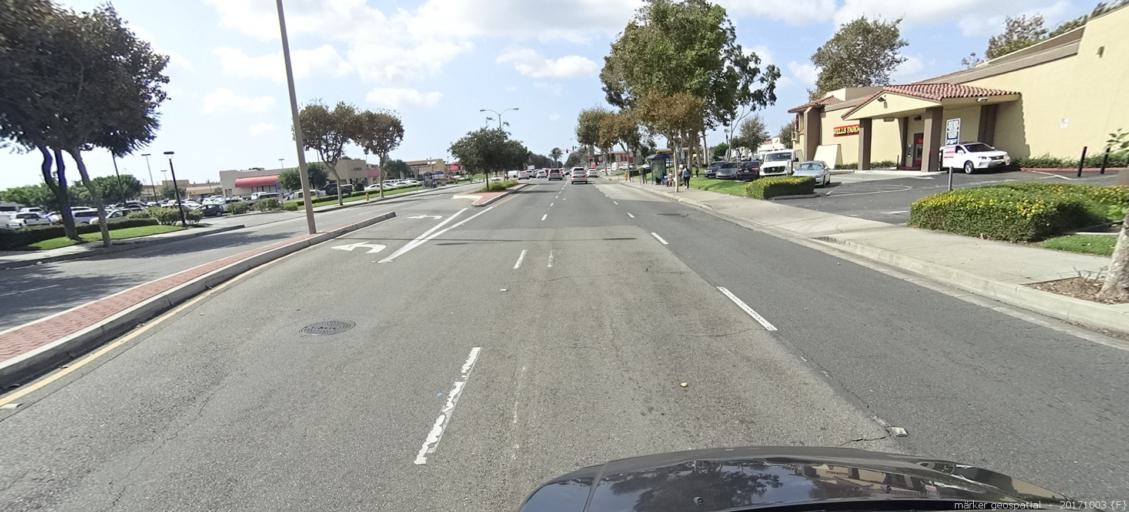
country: US
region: California
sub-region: Orange County
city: Garden Grove
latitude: 33.7745
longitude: -117.9184
